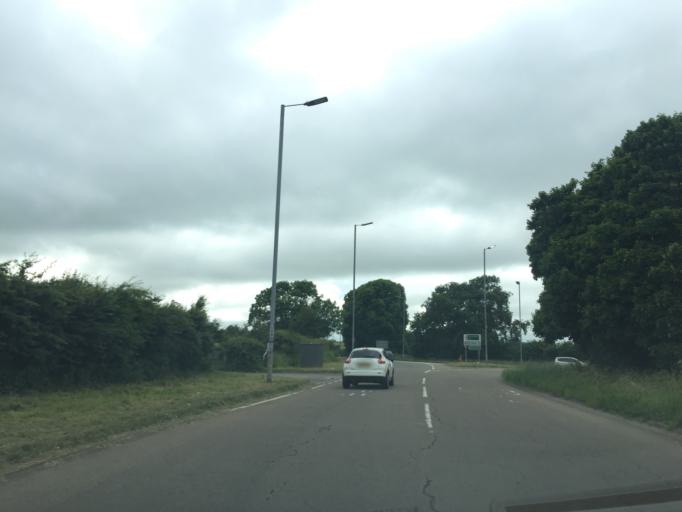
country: GB
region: England
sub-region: Dorset
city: Lytchett Matravers
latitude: 50.7865
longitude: -2.0729
